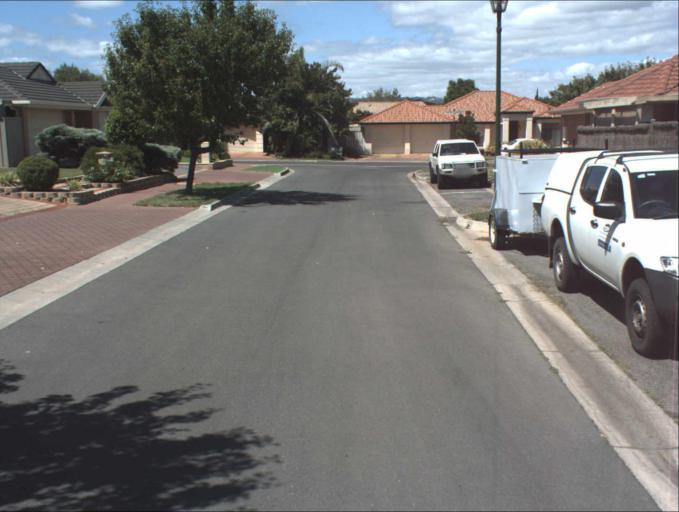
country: AU
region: South Australia
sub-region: Port Adelaide Enfield
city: Gilles Plains
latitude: -34.8531
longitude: 138.6462
